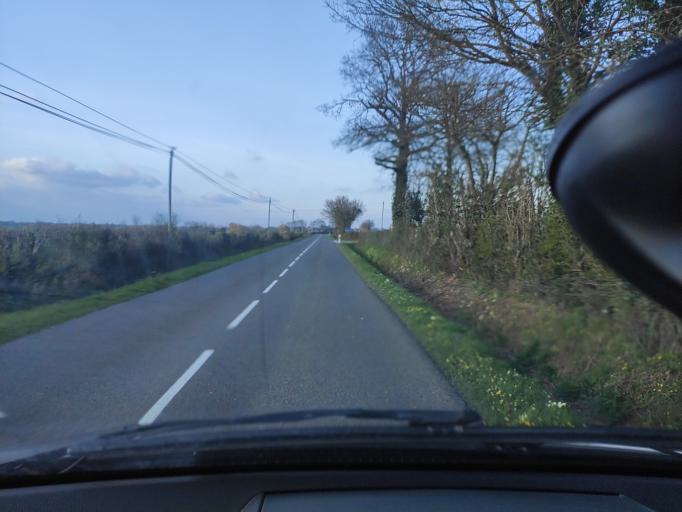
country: FR
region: Pays de la Loire
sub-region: Departement de la Vendee
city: La Chaize-le-Vicomte
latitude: 46.6432
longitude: -1.2985
